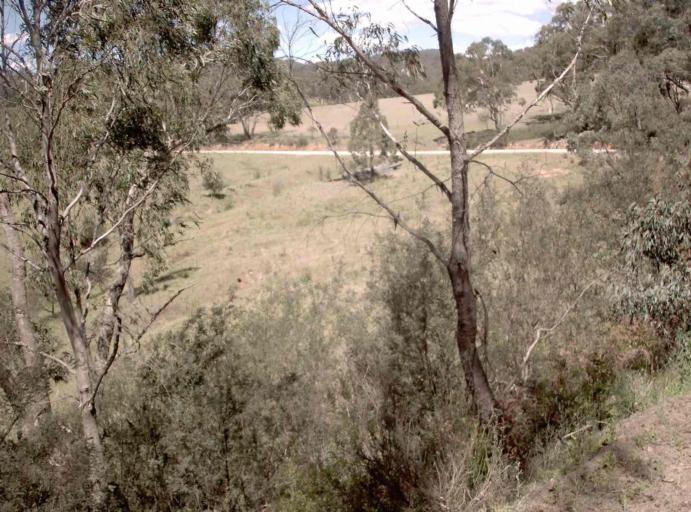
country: AU
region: New South Wales
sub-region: Snowy River
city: Jindabyne
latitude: -37.0395
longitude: 148.5549
